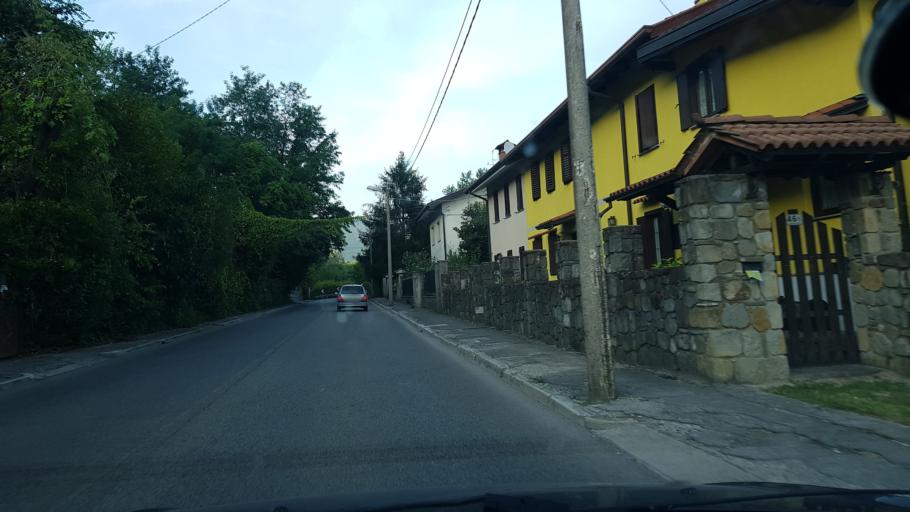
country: IT
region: Friuli Venezia Giulia
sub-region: Provincia di Gorizia
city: Gorizia
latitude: 45.9524
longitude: 13.6055
